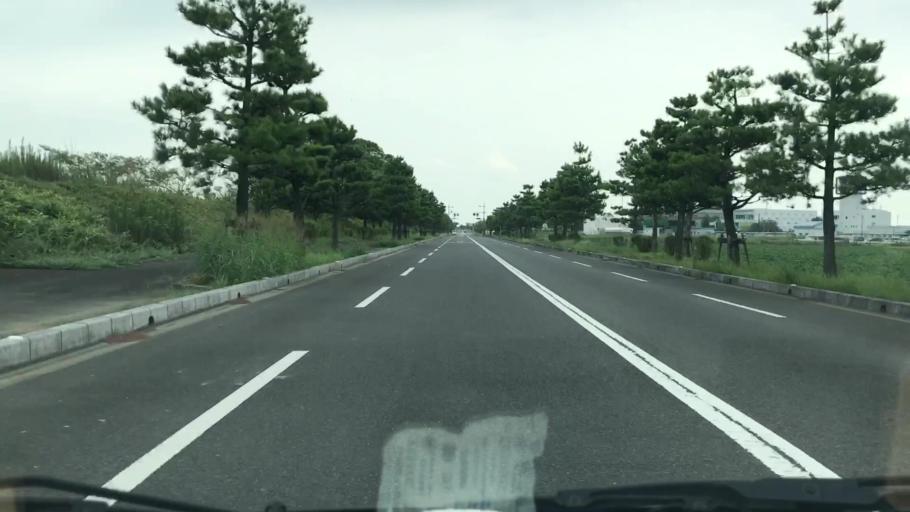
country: JP
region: Saga Prefecture
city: Okawa
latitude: 33.1564
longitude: 130.2990
